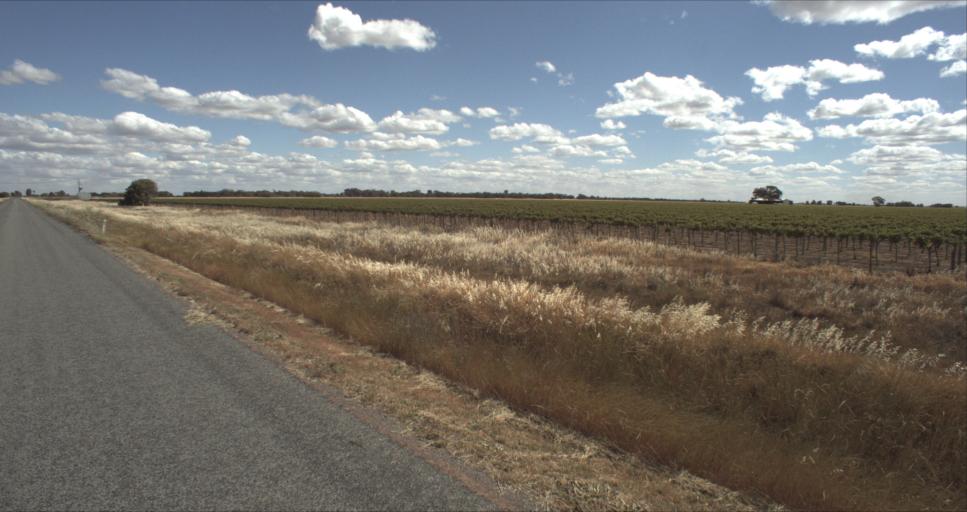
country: AU
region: New South Wales
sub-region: Leeton
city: Leeton
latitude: -34.4951
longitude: 146.2465
